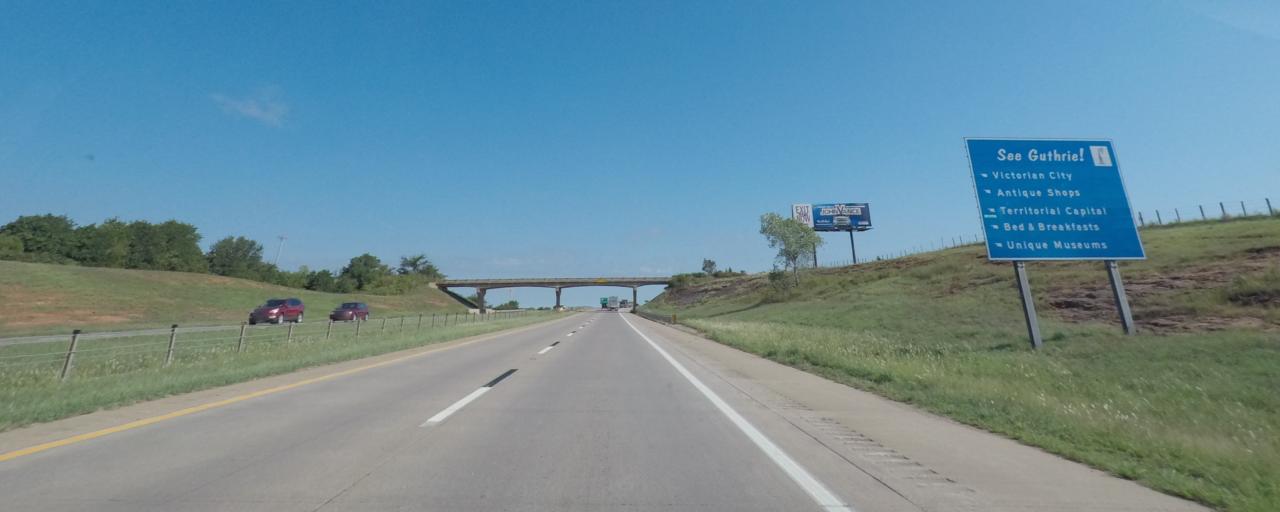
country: US
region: Oklahoma
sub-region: Logan County
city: Guthrie
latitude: 35.8112
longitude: -97.4162
